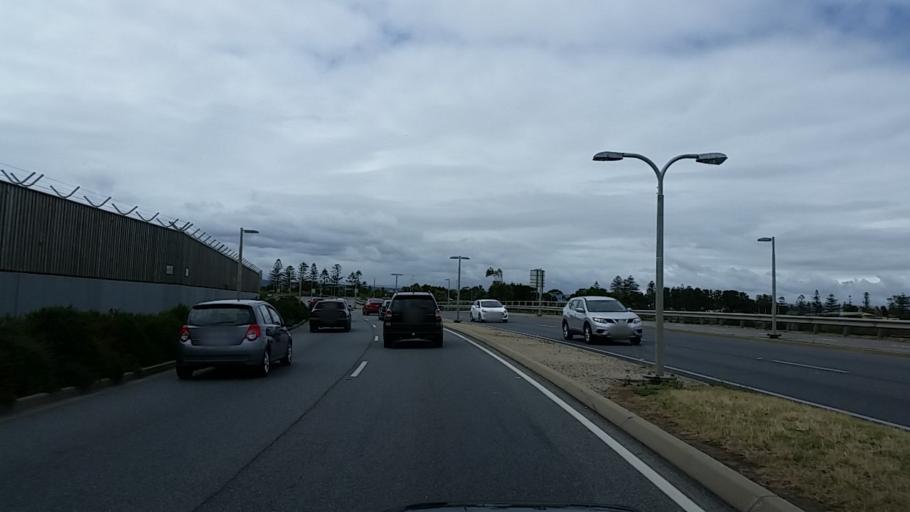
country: AU
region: South Australia
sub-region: Adelaide
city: Glenelg
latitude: -34.9596
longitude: 138.5145
